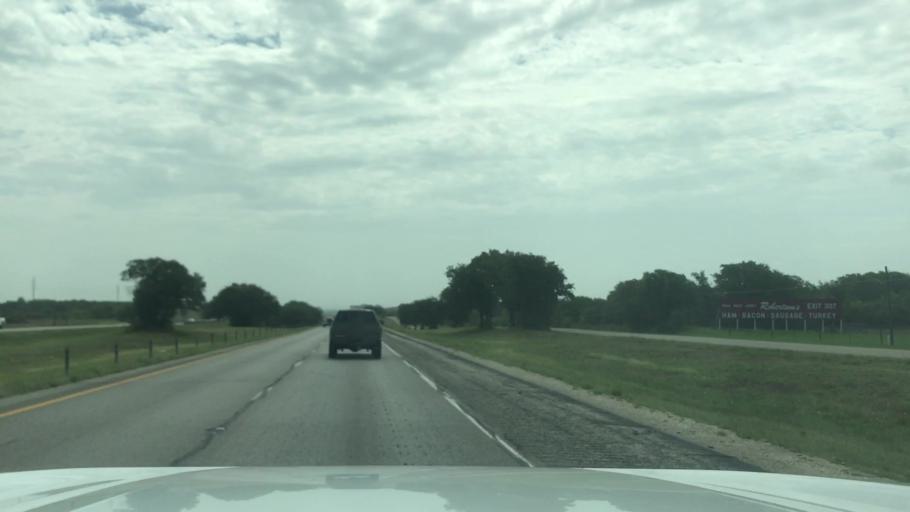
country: US
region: Texas
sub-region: Callahan County
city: Baird
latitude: 32.4054
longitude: -99.4387
